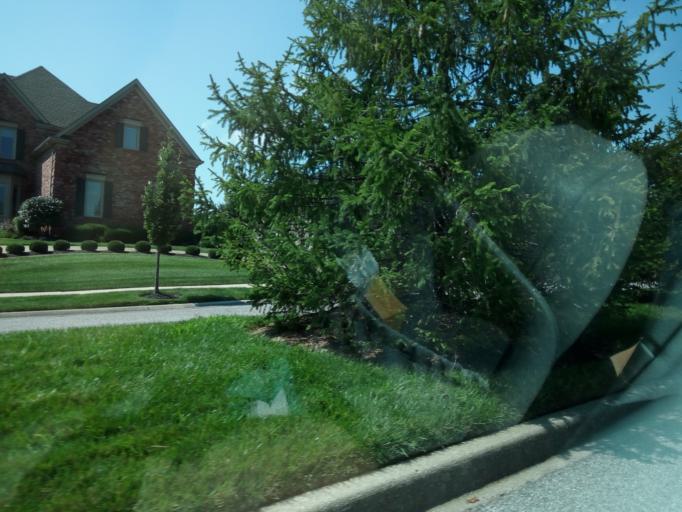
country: US
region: Kentucky
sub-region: Oldham County
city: Pewee Valley
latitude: 38.2744
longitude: -85.4841
